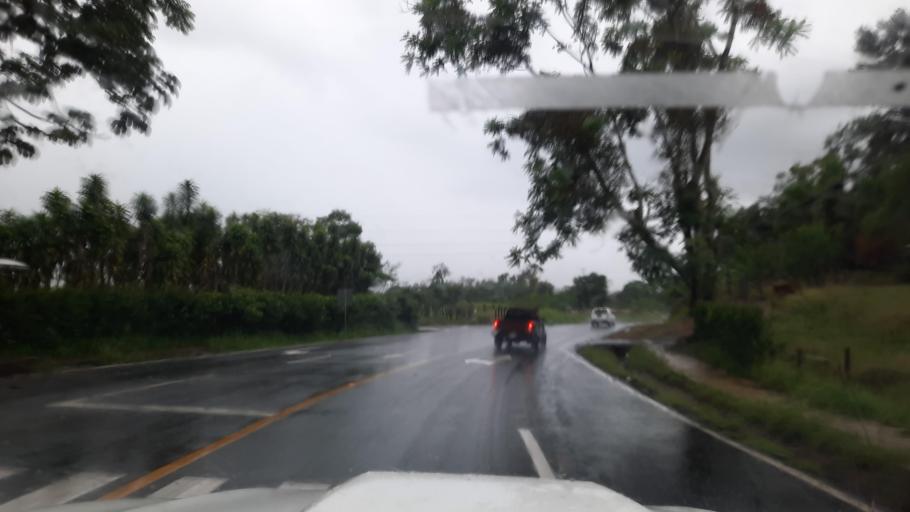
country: PA
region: Chiriqui
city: Sortova
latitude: 8.5619
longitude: -82.6281
